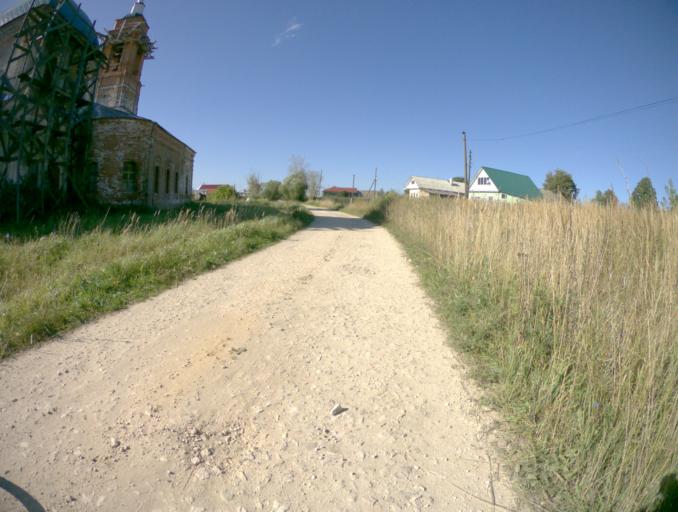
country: RU
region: Vladimir
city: Kameshkovo
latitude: 56.3619
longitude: 40.8935
